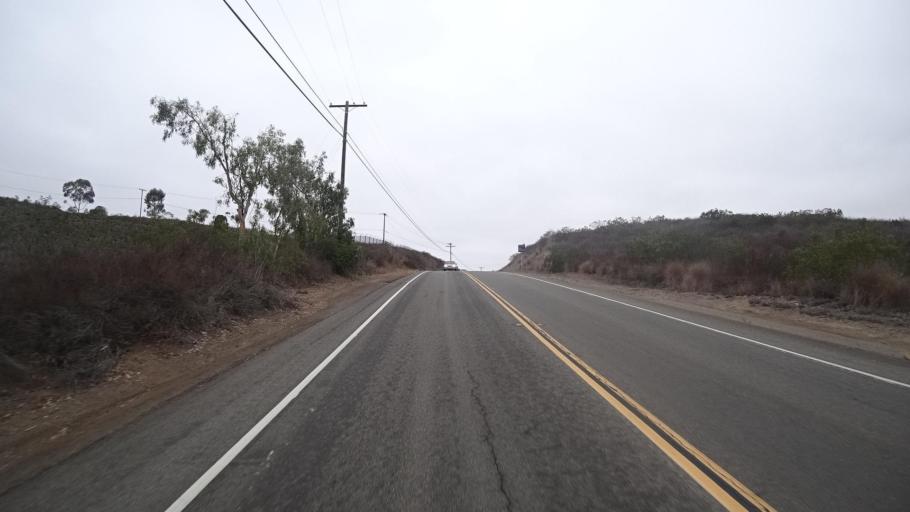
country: US
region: California
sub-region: San Diego County
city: Lake San Marcos
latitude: 33.0907
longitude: -117.1907
